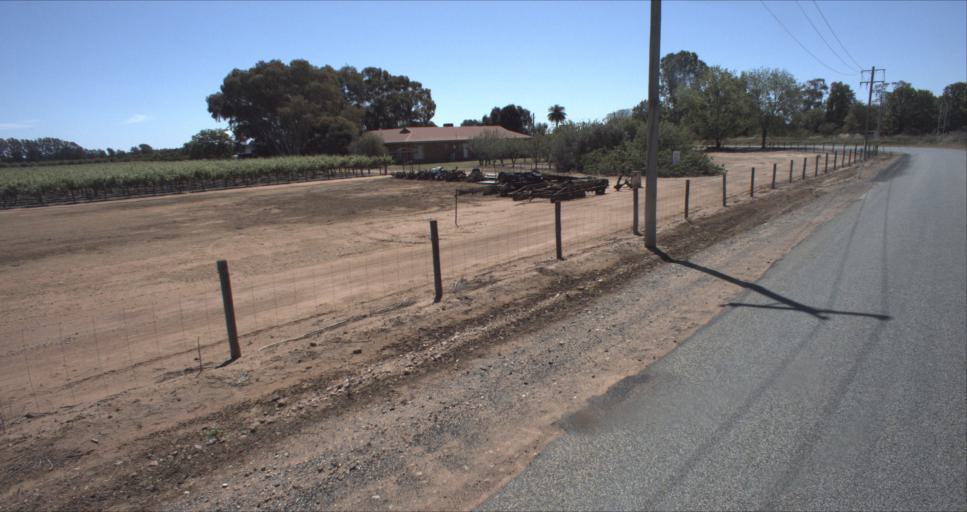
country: AU
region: New South Wales
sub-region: Leeton
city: Leeton
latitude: -34.5503
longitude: 146.3724
